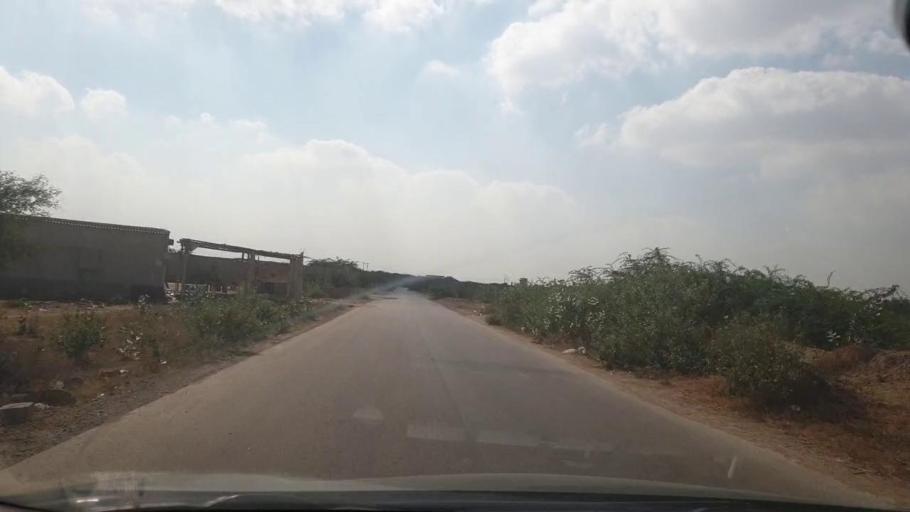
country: PK
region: Sindh
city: Malir Cantonment
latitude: 25.0174
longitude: 67.3535
